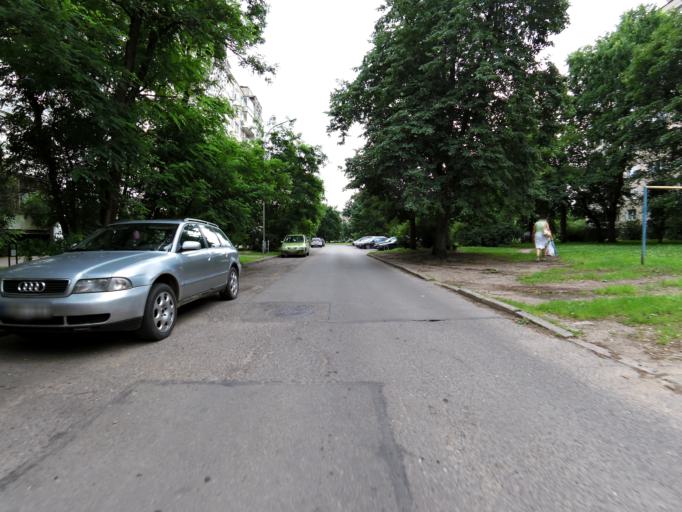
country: LT
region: Vilnius County
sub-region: Vilnius
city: Vilnius
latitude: 54.6995
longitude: 25.2961
